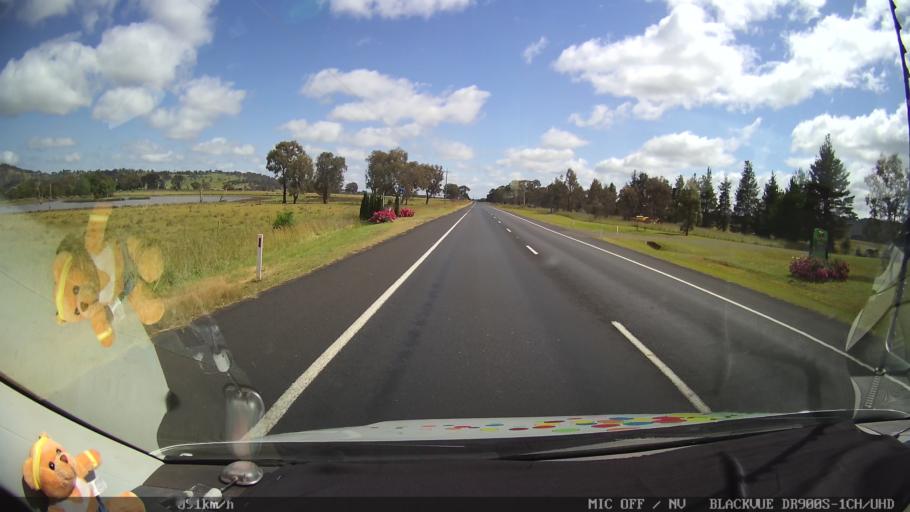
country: AU
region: New South Wales
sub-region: Glen Innes Severn
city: Glen Innes
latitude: -29.8747
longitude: 151.7347
